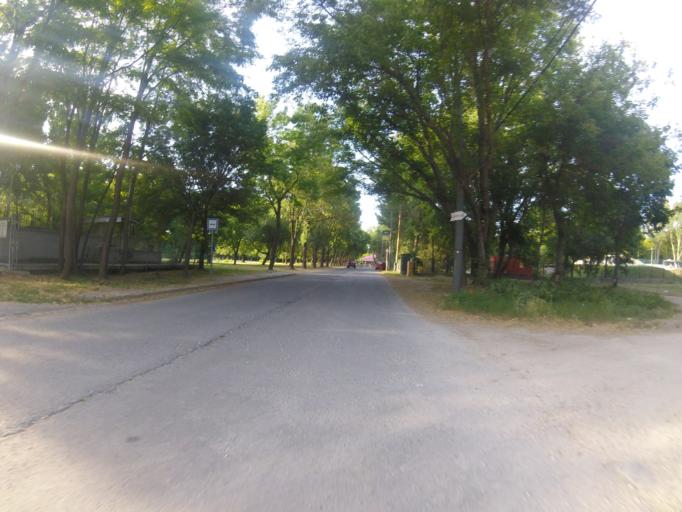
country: HU
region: Budapest
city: Budapest III. keruelet
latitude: 47.5503
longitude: 19.0567
